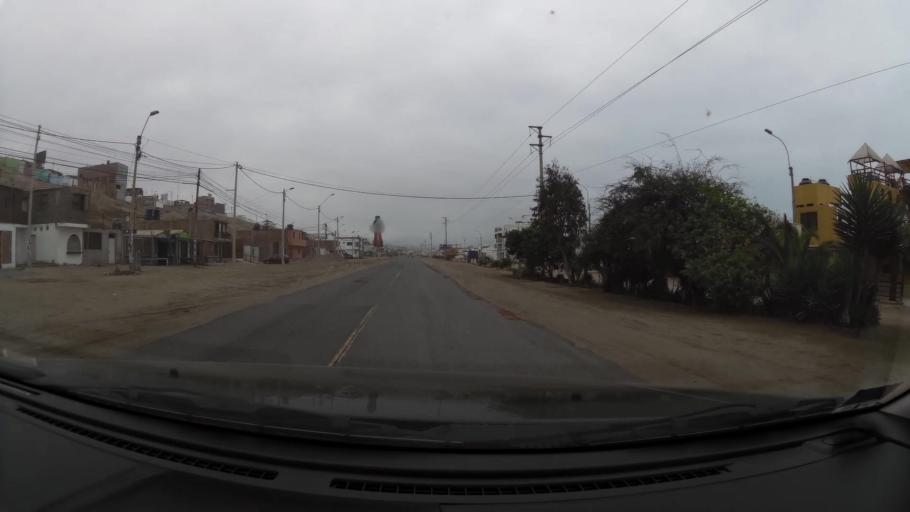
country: PE
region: Lima
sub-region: Lima
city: Punta Hermosa
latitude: -12.3560
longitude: -76.8043
